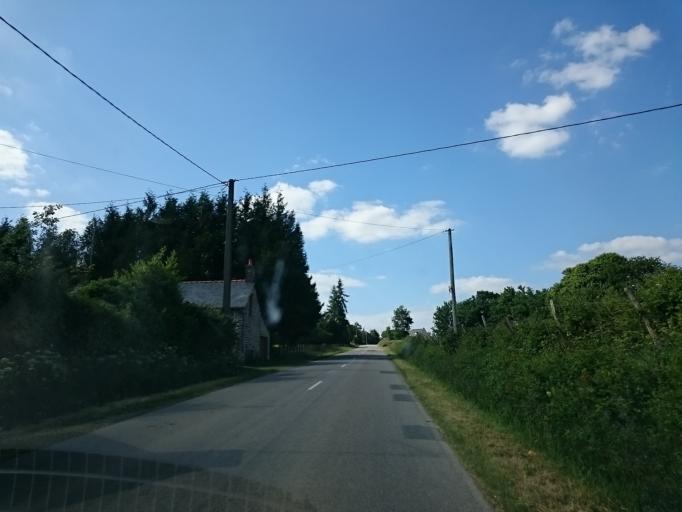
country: FR
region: Brittany
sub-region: Departement d'Ille-et-Vilaine
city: Chanteloup
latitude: 47.9602
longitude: -1.6150
